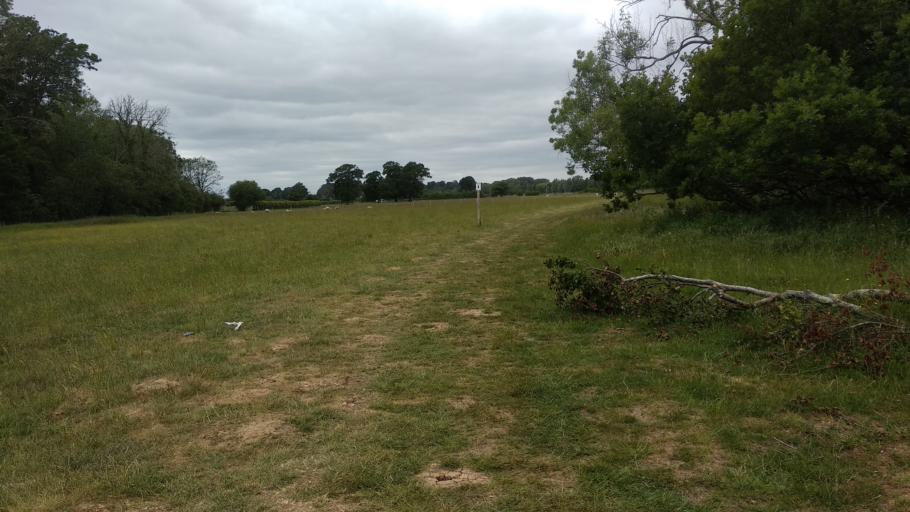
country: GB
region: England
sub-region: Kent
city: Ashford
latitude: 51.1533
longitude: 0.8340
